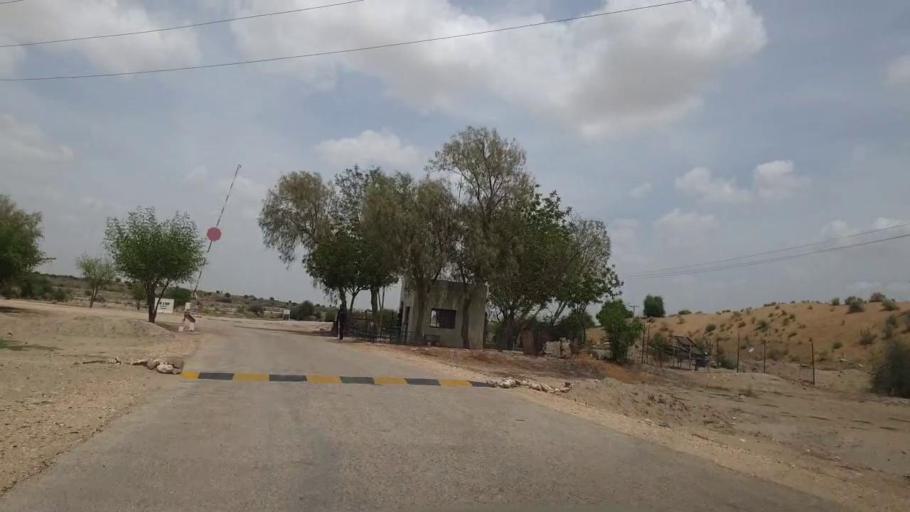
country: PK
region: Sindh
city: Kot Diji
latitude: 27.1986
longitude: 69.1531
